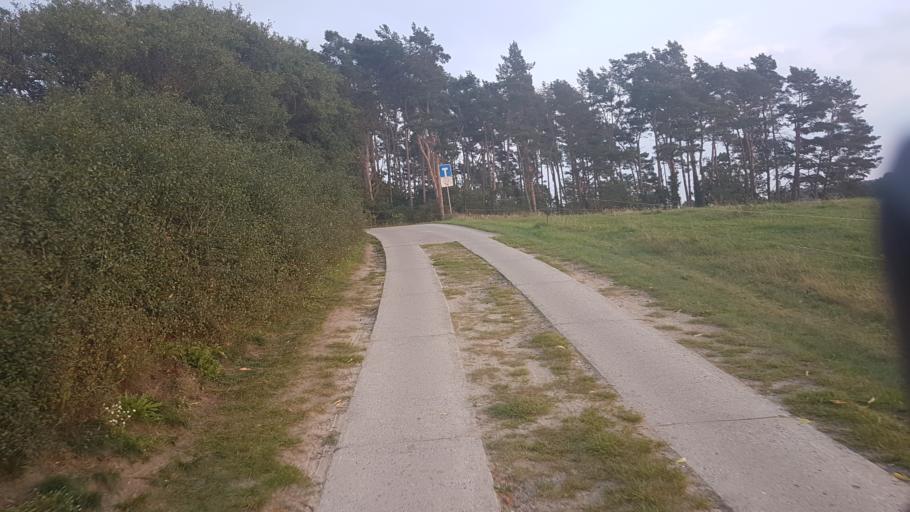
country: DE
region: Mecklenburg-Vorpommern
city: Putbus
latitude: 54.3502
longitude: 13.5310
